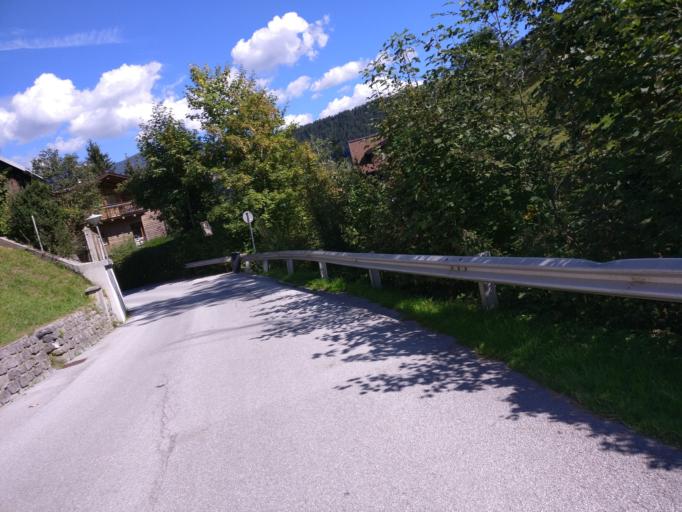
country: AT
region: Salzburg
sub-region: Politischer Bezirk Sankt Johann im Pongau
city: Bischofshofen
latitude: 47.4149
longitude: 13.2125
